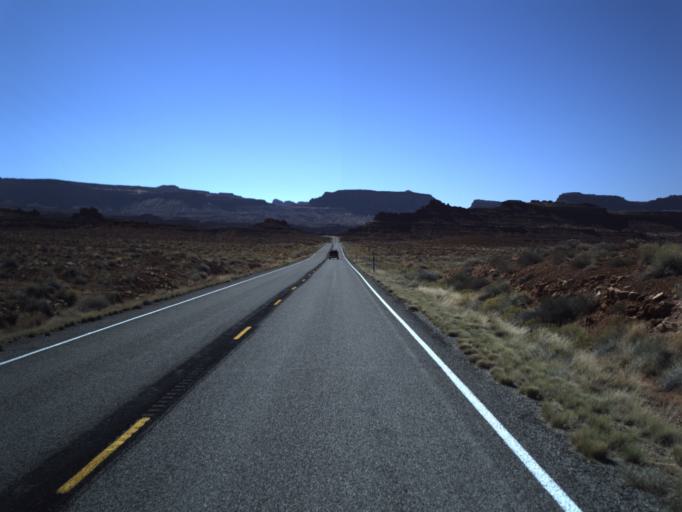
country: US
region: Utah
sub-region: San Juan County
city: Blanding
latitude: 37.8416
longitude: -110.3558
